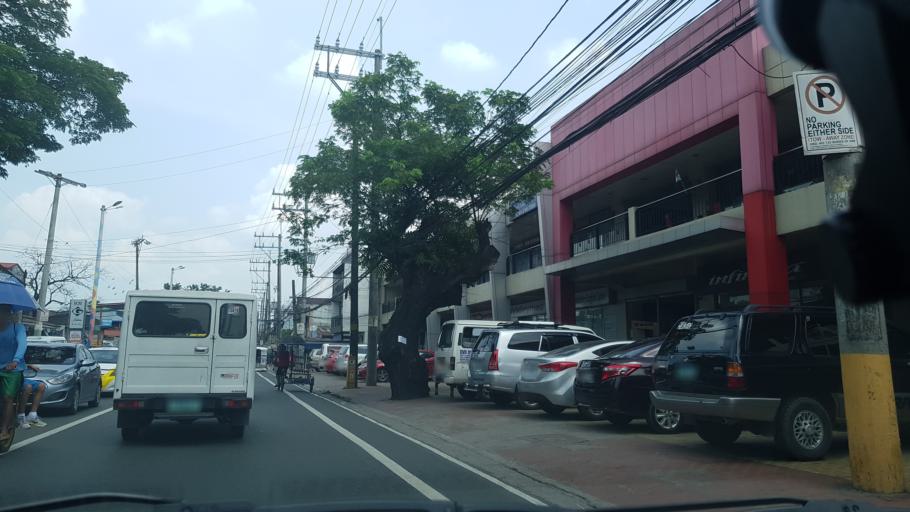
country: PH
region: Calabarzon
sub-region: Province of Rizal
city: San Mateo
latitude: 14.6702
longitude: 121.1085
